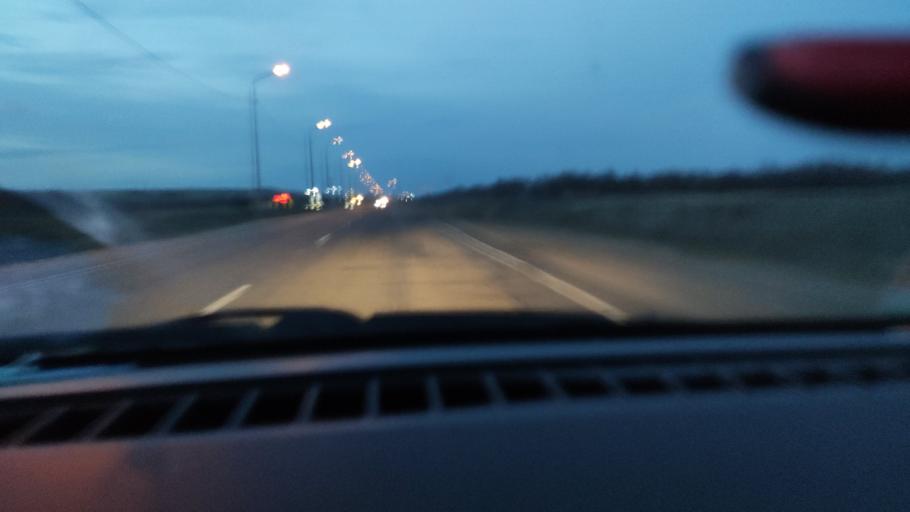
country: RU
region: Saratov
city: Sinodskoye
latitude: 52.0830
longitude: 46.7982
